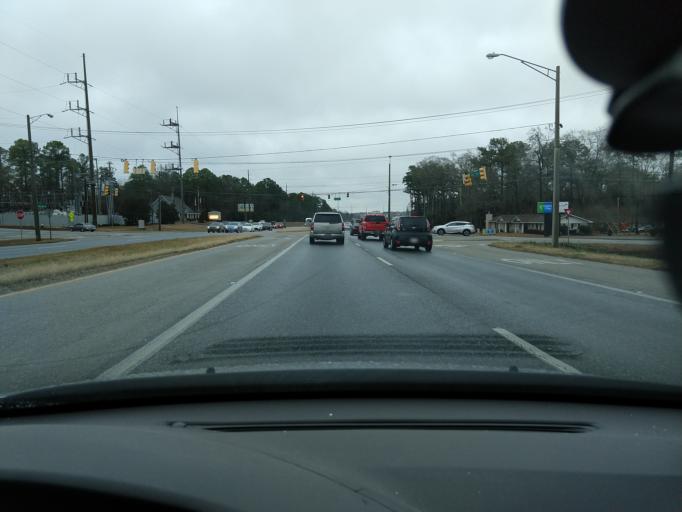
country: US
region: Alabama
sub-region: Houston County
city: Dothan
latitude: 31.2370
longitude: -85.4316
